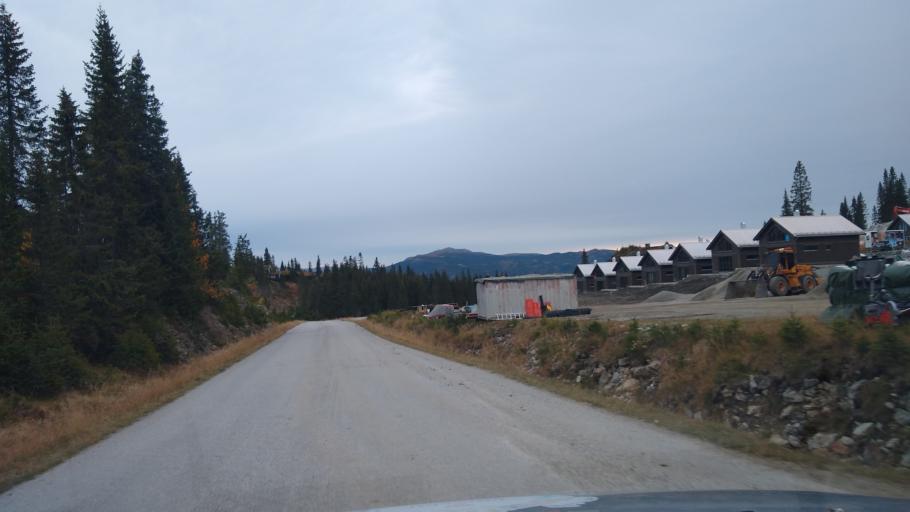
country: NO
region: Oppland
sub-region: Ringebu
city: Ringebu
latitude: 61.4738
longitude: 10.1303
